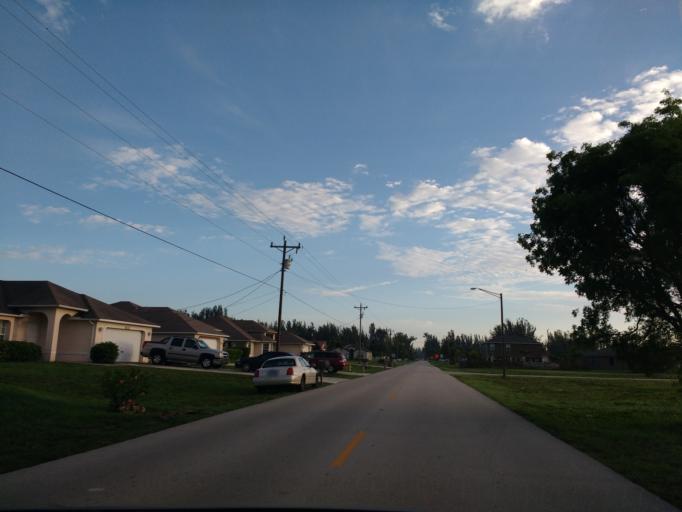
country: US
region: Florida
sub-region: Lee County
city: Cape Coral
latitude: 26.6274
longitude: -82.0154
